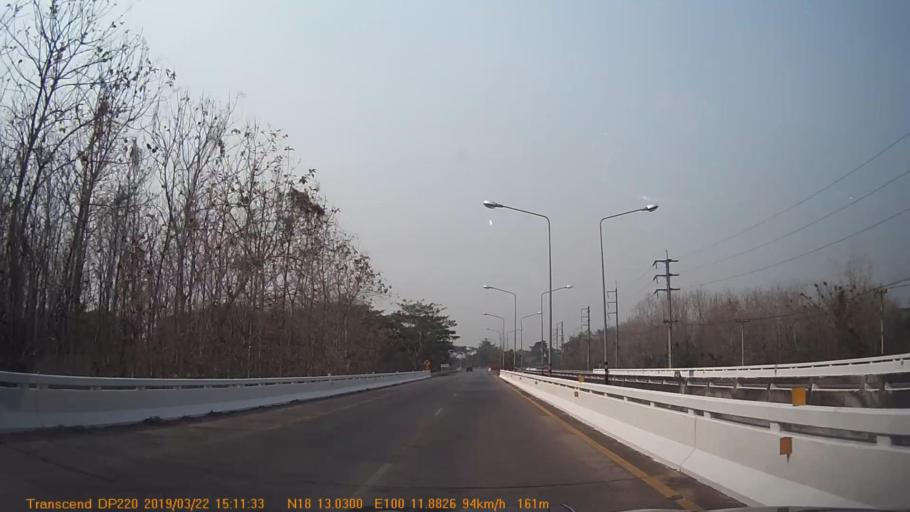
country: TH
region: Phrae
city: Nong Muang Khai
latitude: 18.2177
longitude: 100.1980
